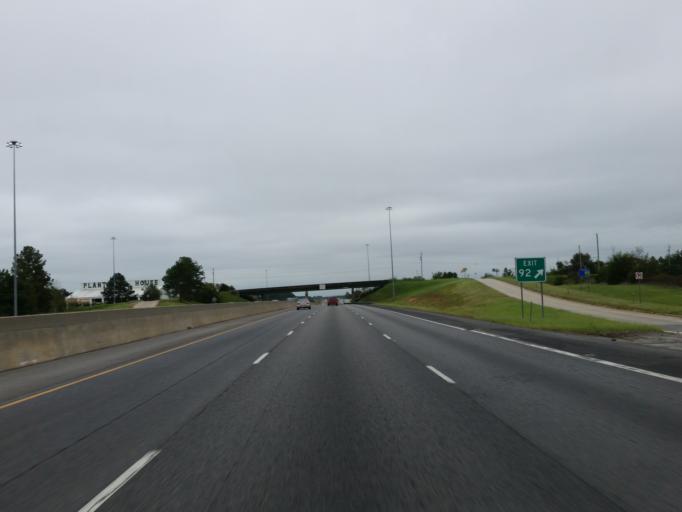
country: US
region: Georgia
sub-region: Crisp County
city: Cordele
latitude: 31.8383
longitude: -83.7147
